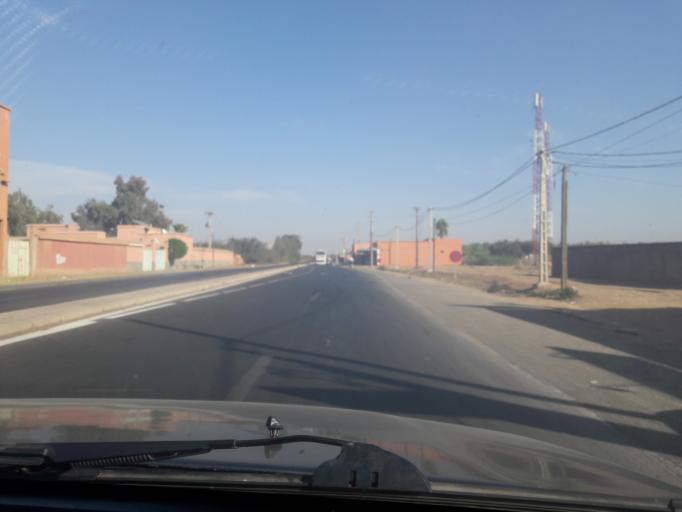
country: MA
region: Marrakech-Tensift-Al Haouz
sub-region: Marrakech
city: Marrakesh
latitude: 31.6472
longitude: -7.9019
